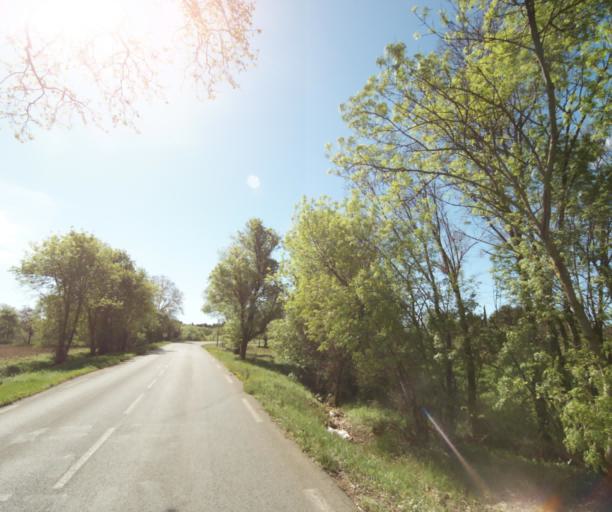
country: FR
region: Languedoc-Roussillon
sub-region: Departement de l'Herault
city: Villeneuve-les-Maguelone
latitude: 43.5464
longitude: 3.8474
